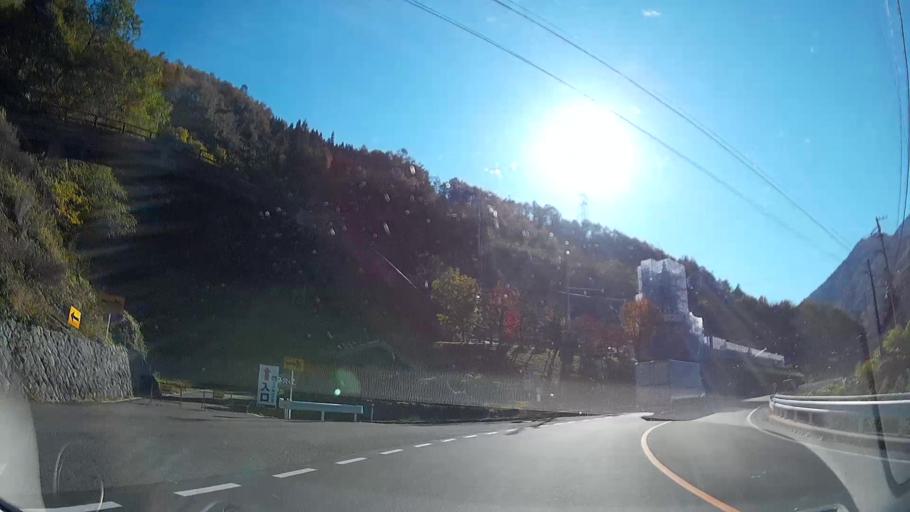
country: JP
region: Nagano
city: Toyoshina
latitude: 36.1539
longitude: 137.7531
